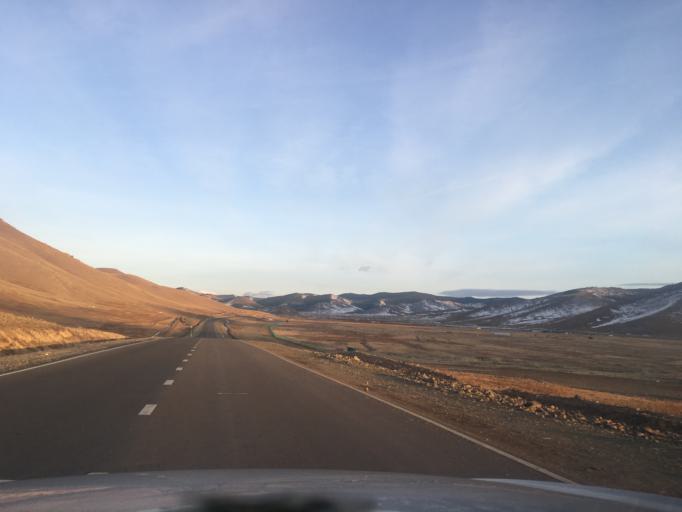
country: MN
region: Central Aimak
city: Mandal
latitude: 48.1158
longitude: 106.6958
